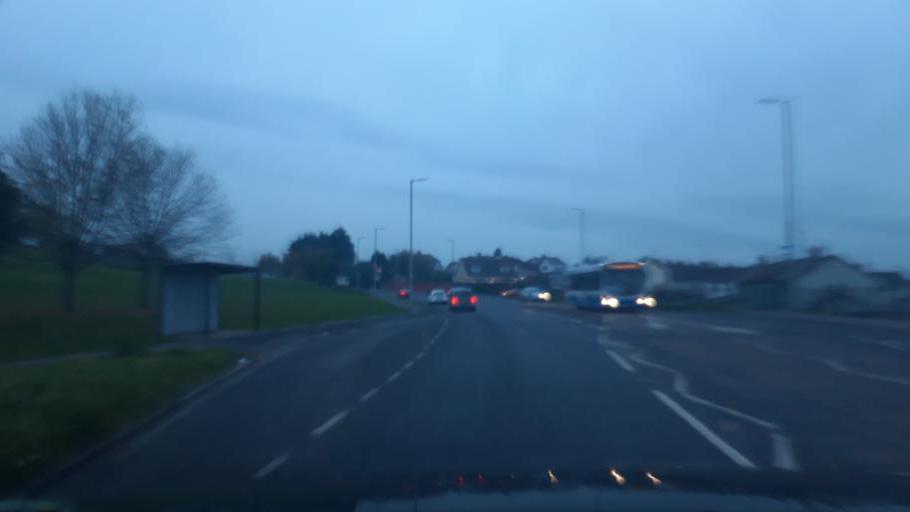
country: GB
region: Northern Ireland
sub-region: Newry and Mourne District
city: Newry
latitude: 54.1842
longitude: -6.3562
